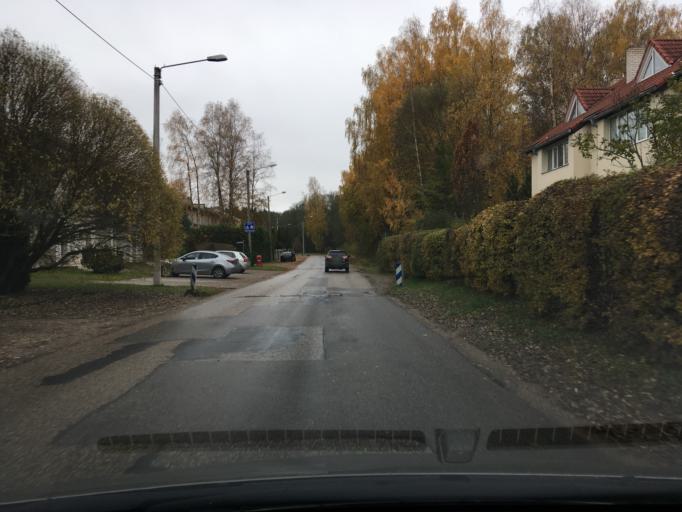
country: EE
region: Tartu
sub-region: Tartu linn
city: Tartu
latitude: 58.3580
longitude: 26.7788
